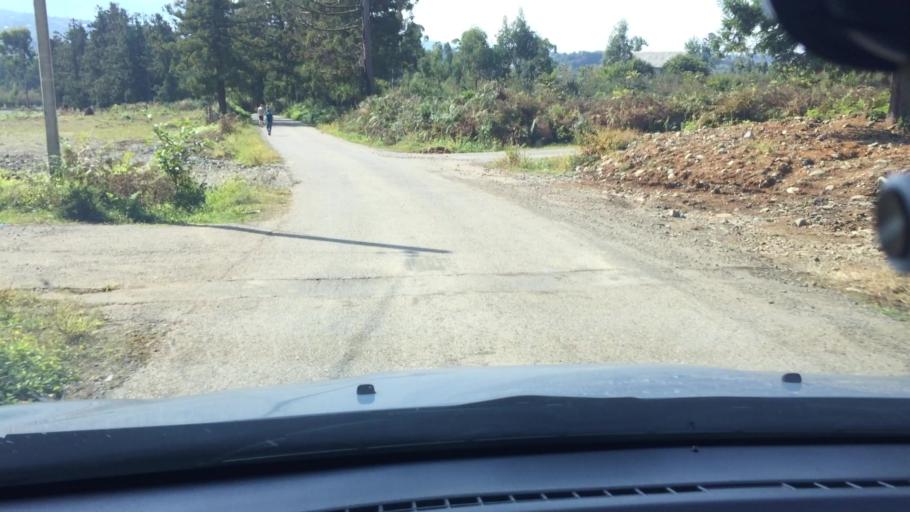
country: GE
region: Ajaria
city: Kobuleti
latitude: 41.8087
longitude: 41.8236
